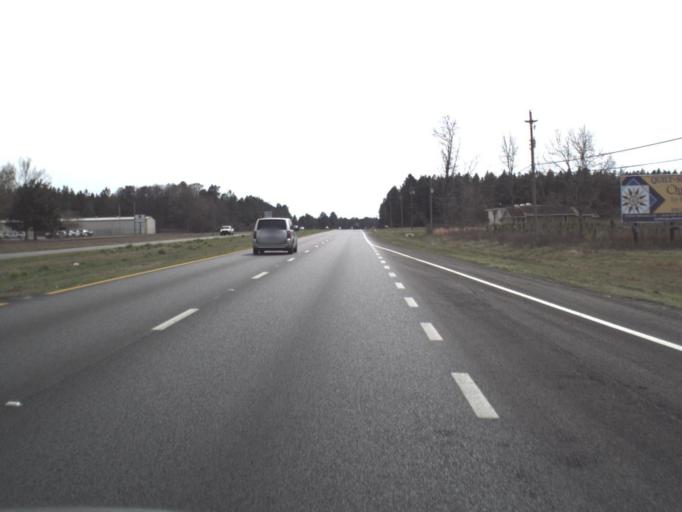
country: US
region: Florida
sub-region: Bay County
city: Youngstown
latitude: 30.3487
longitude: -85.4404
